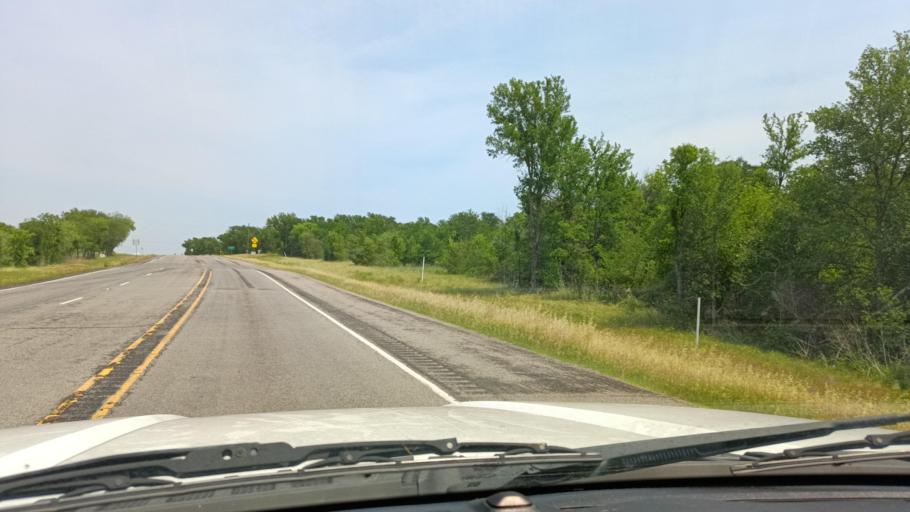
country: US
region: Texas
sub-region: Bell County
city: Rogers
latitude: 30.8777
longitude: -97.1414
